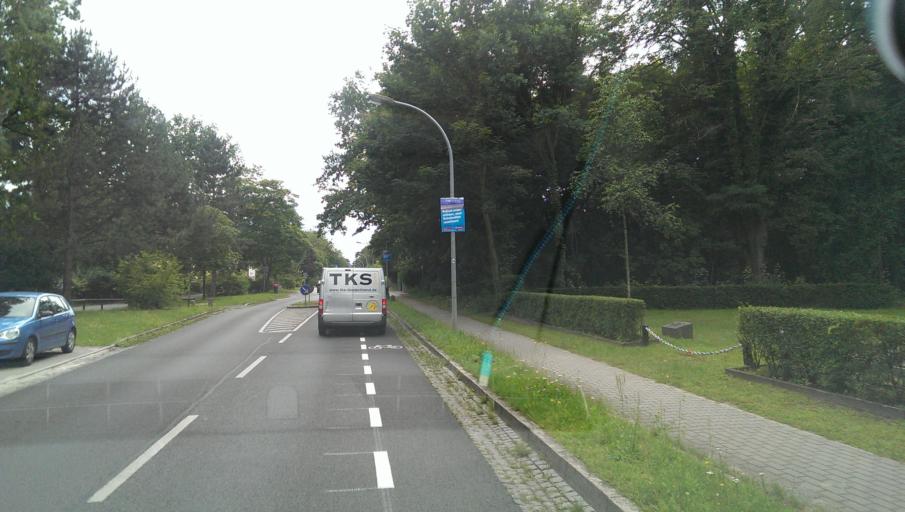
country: DE
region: Brandenburg
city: Kleinmachnow
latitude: 52.4121
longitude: 13.2210
